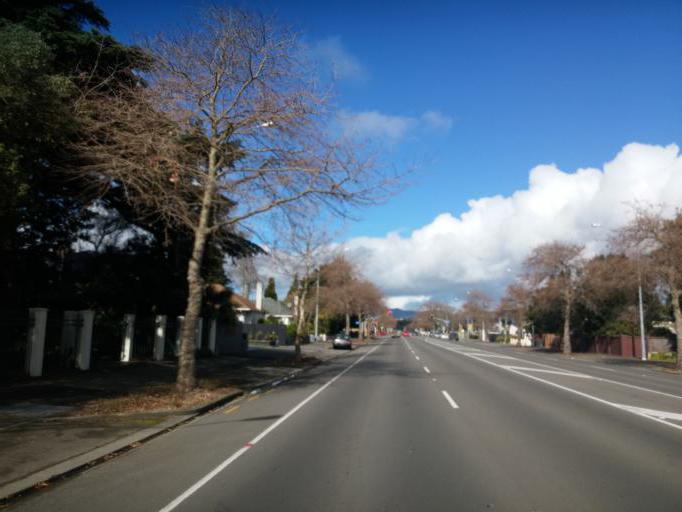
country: NZ
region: Manawatu-Wanganui
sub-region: Palmerston North City
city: Palmerston North
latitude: -40.3635
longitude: 175.6169
